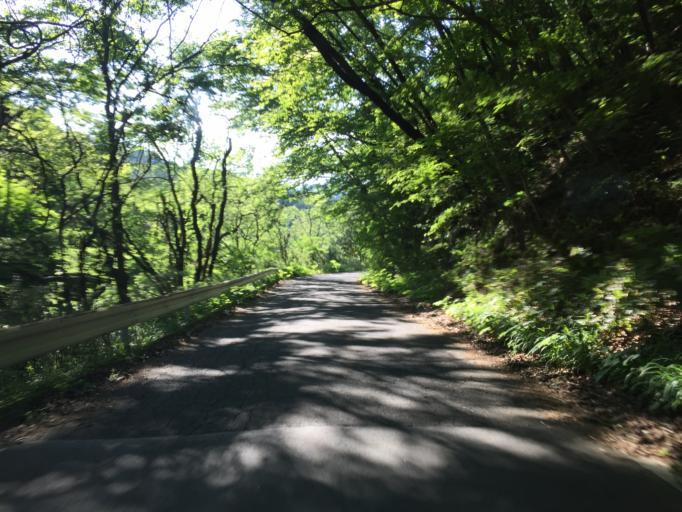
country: JP
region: Ibaraki
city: Kitaibaraki
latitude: 36.8761
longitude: 140.6664
